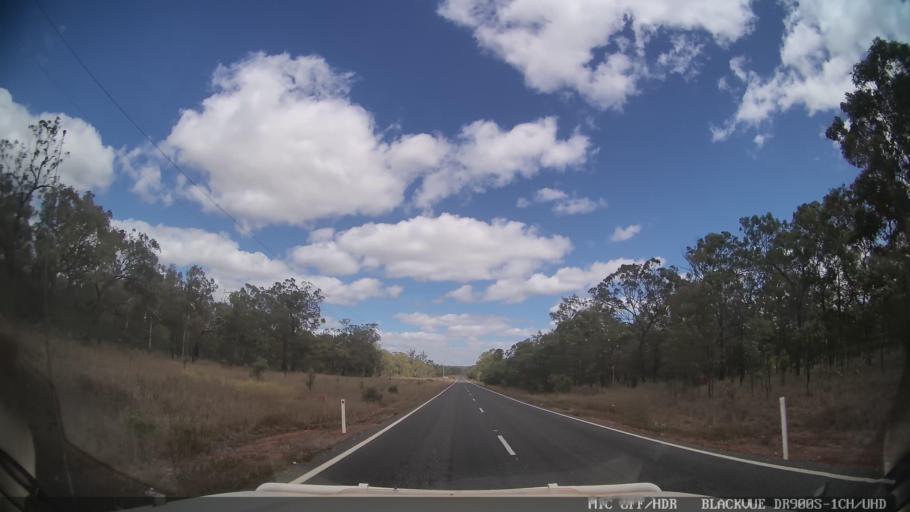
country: AU
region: Queensland
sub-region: Tablelands
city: Ravenshoe
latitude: -18.0255
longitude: 144.8702
